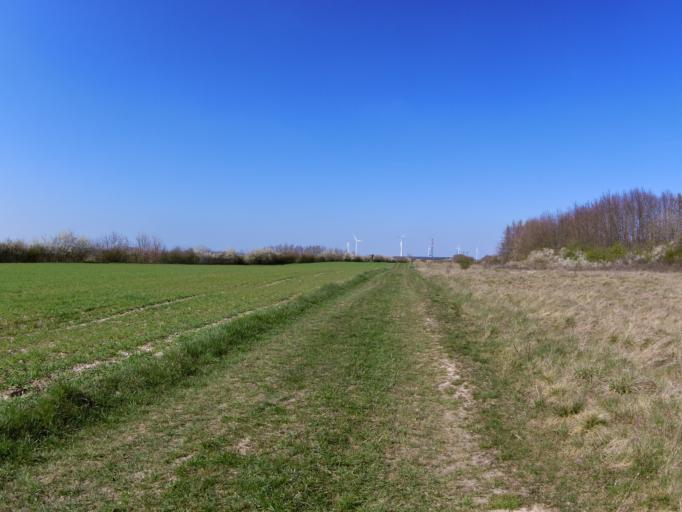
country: DE
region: Bavaria
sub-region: Regierungsbezirk Unterfranken
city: Sulzfeld am Main
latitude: 49.7298
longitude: 10.1048
